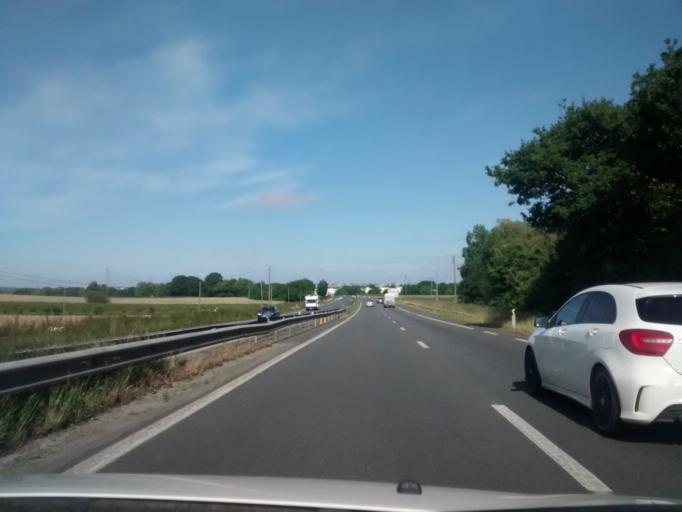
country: FR
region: Brittany
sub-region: Departement des Cotes-d'Armor
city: Pommeret
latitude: 48.4800
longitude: -2.6284
